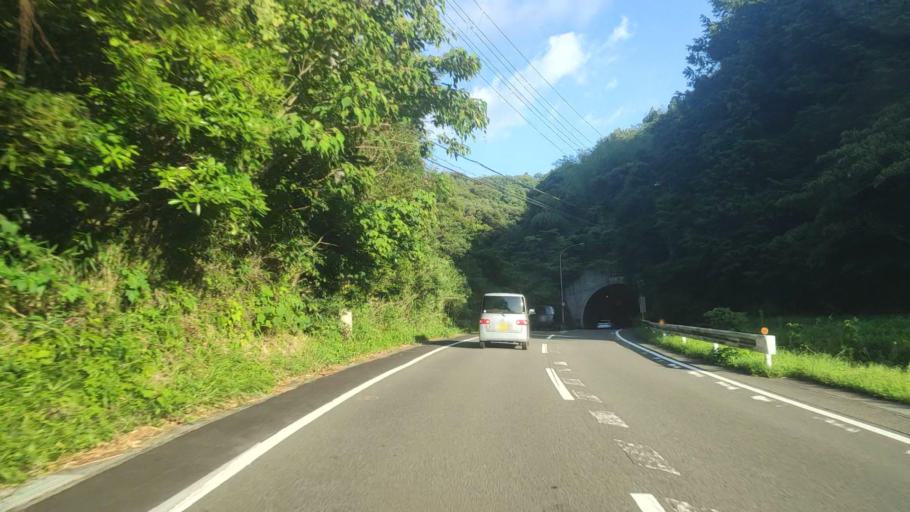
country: JP
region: Wakayama
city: Tanabe
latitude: 33.7314
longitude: 135.4342
